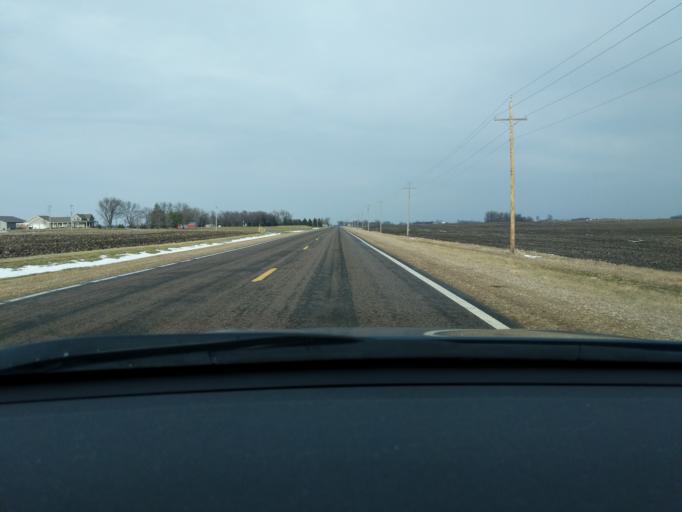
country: US
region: Minnesota
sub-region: Renville County
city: Renville
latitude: 44.7637
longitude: -95.3409
